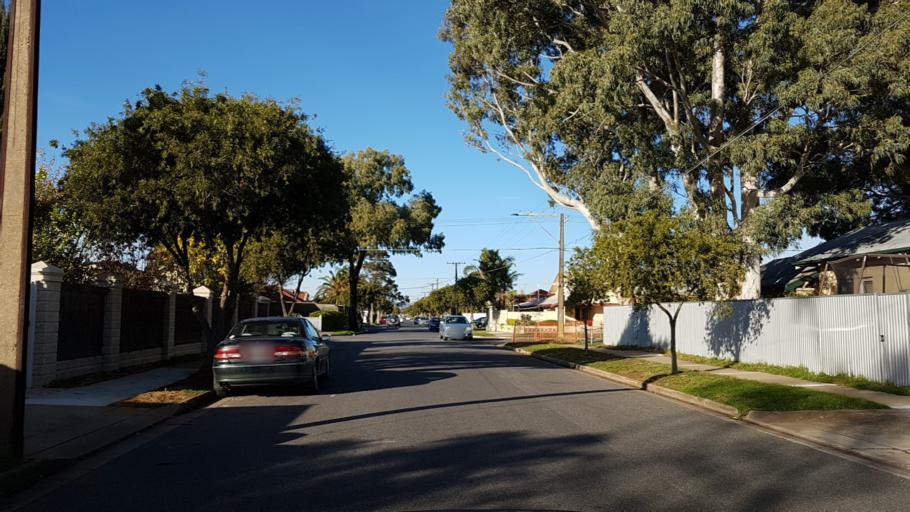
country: AU
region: South Australia
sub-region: Charles Sturt
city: Woodville North
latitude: -34.8678
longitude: 138.5433
